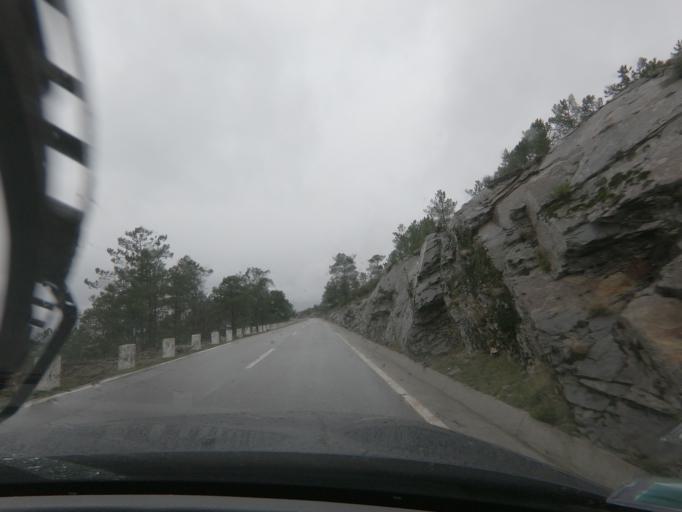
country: PT
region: Vila Real
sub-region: Mondim de Basto
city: Mondim de Basto
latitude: 41.3358
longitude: -7.8768
